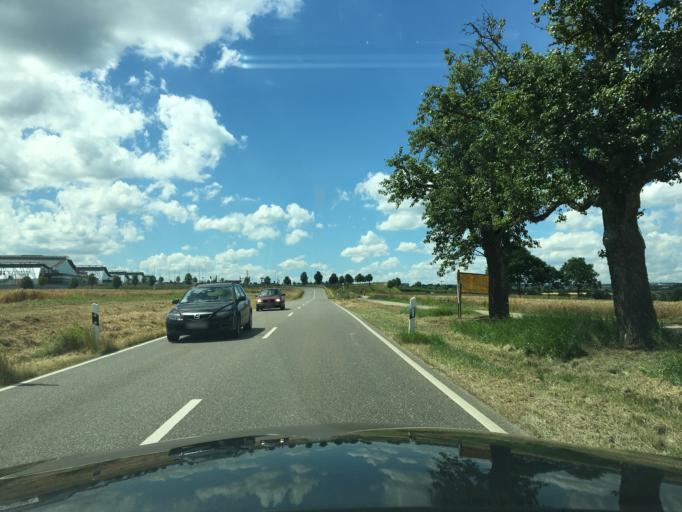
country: DE
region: Baden-Wuerttemberg
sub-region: Regierungsbezirk Stuttgart
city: Leinfelden-Echterdingen
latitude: 48.6989
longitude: 9.1951
